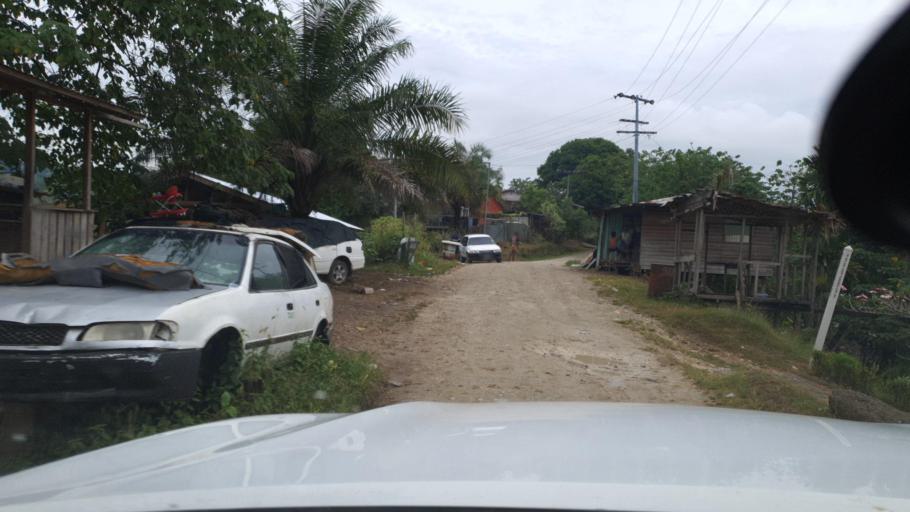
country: SB
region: Guadalcanal
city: Honiara
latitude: -9.4471
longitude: 159.9838
